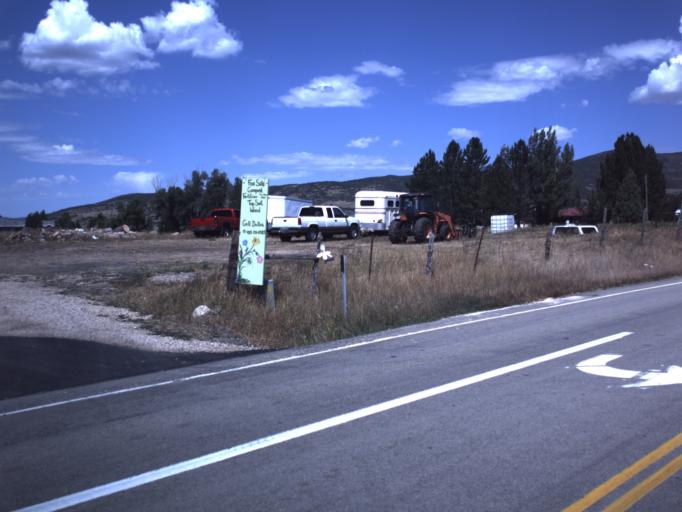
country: US
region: Utah
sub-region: Summit County
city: Oakley
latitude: 40.7207
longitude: -111.3003
